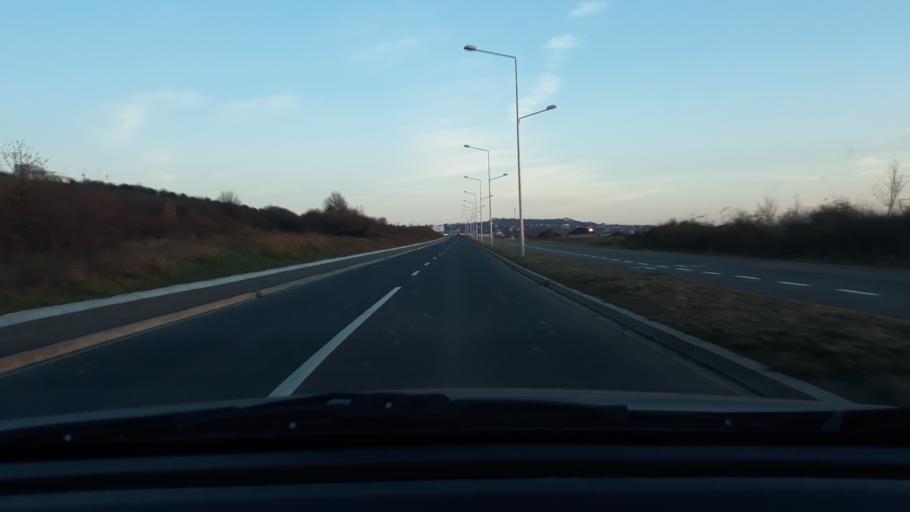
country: RO
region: Bihor
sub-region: Comuna Biharea
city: Oradea
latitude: 47.0997
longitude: 21.9166
